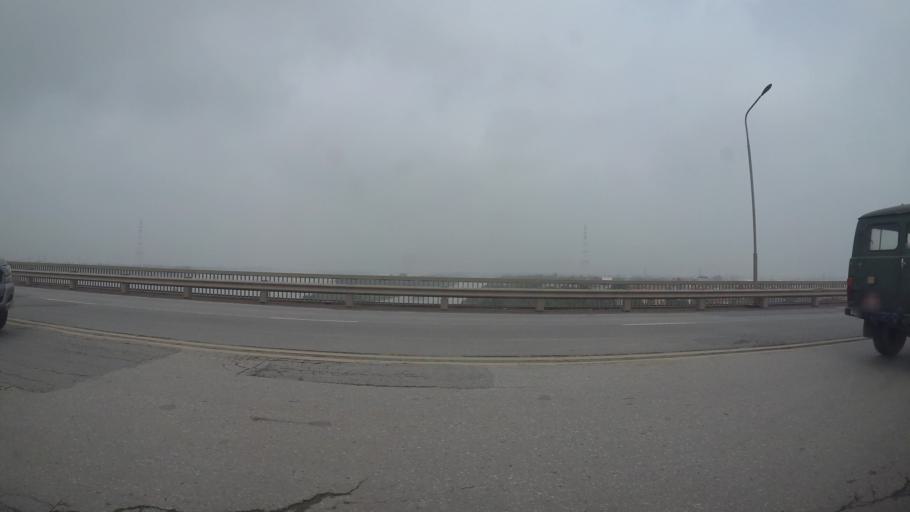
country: VN
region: Ha Noi
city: Tay Ho
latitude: 21.1012
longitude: 105.7867
